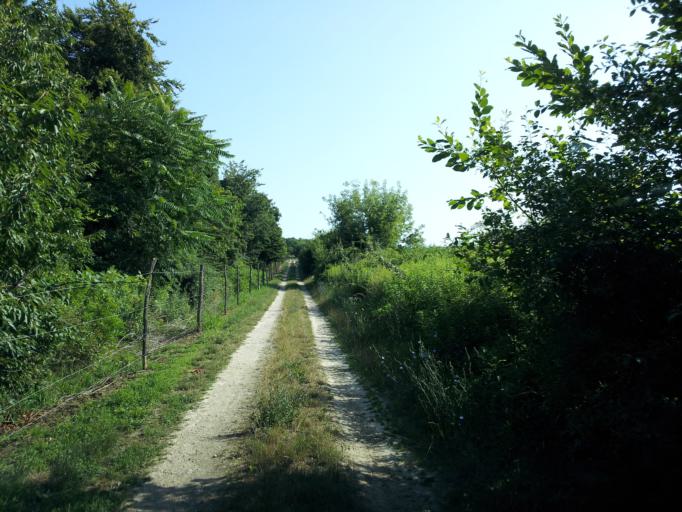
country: HU
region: Zala
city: Cserszegtomaj
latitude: 46.8544
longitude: 17.2218
